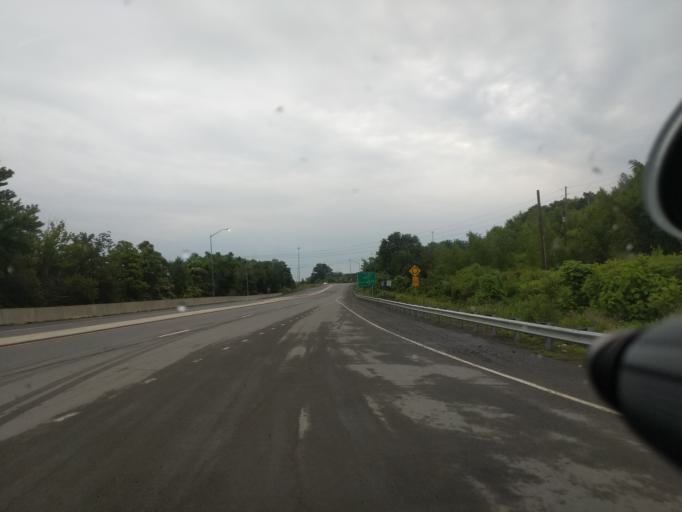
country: US
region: Pennsylvania
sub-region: Luzerne County
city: Dupont
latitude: 41.3318
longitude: -75.7416
